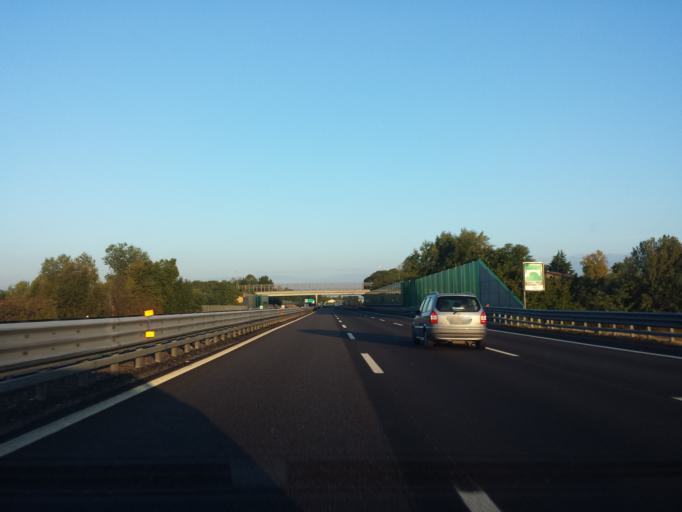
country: IT
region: Lombardy
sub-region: Provincia di Brescia
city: Calcinato
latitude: 45.4654
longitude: 10.4040
